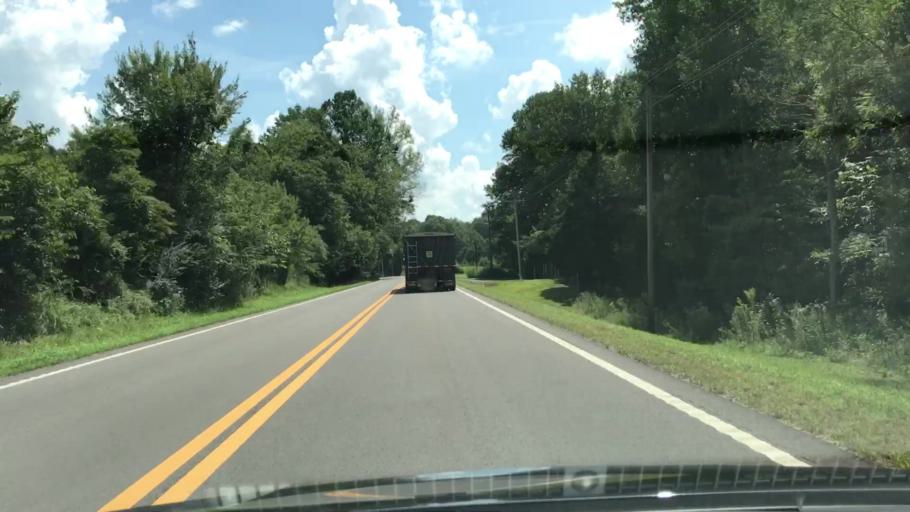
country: US
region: Tennessee
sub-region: Robertson County
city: Springfield
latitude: 36.6167
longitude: -86.9407
